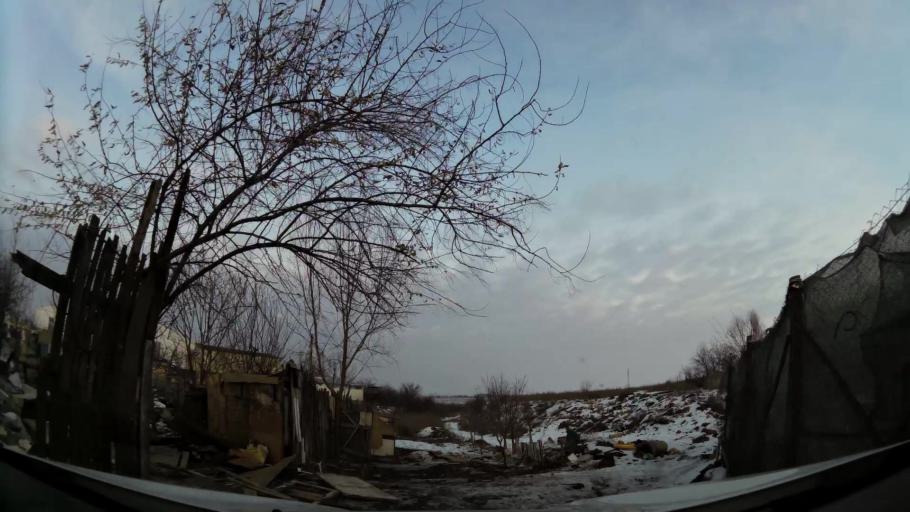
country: RO
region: Ilfov
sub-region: Comuna Popesti-Leordeni
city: Popesti-Leordeni
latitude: 44.3655
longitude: 26.1977
